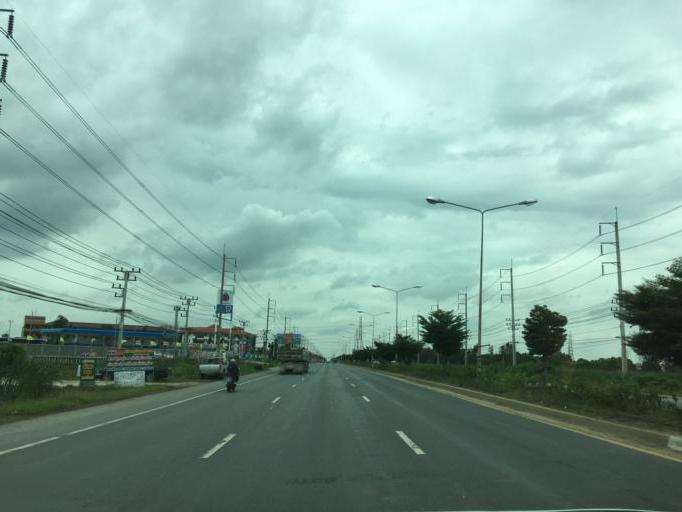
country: TH
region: Phra Nakhon Si Ayutthaya
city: Wang Noi
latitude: 14.2457
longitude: 100.7055
